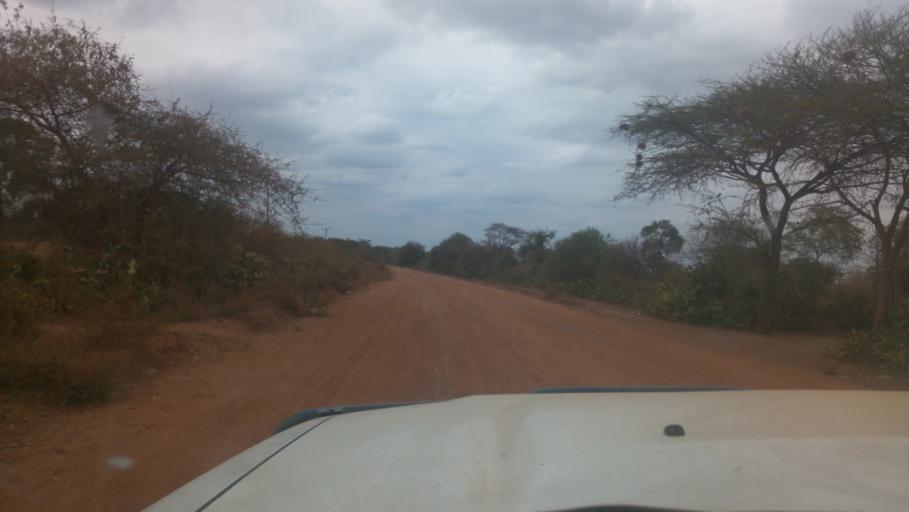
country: KE
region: Kitui
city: Kitui
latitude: -1.5694
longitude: 37.9181
